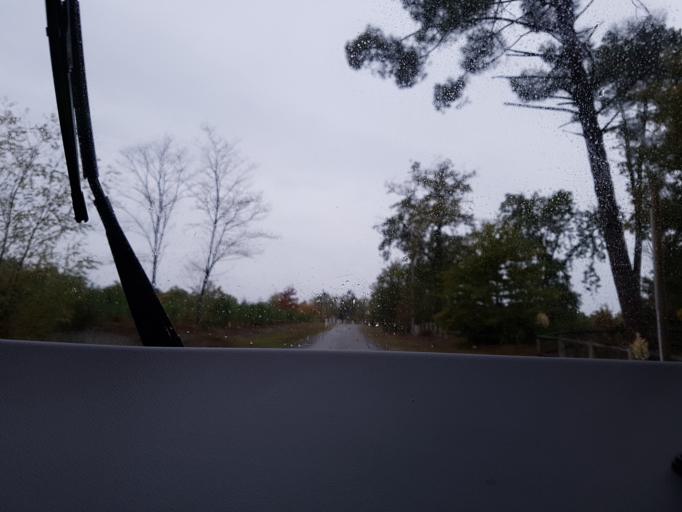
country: FR
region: Aquitaine
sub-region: Departement de la Gironde
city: Saint-Symphorien
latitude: 44.2498
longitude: -0.5034
